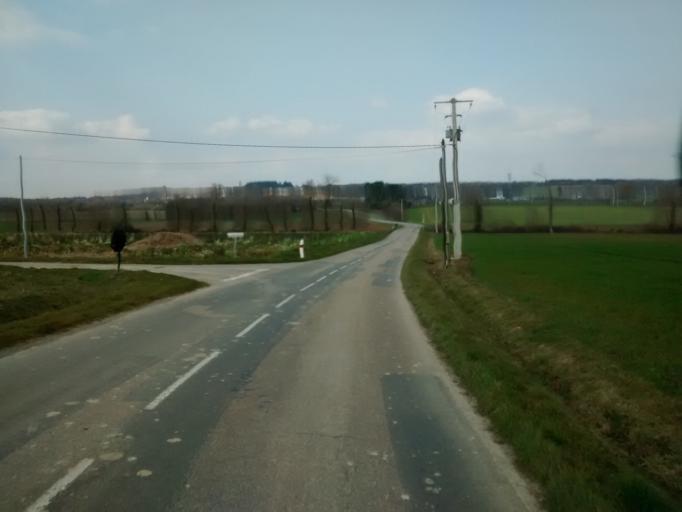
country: FR
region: Brittany
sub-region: Departement d'Ille-et-Vilaine
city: Maure-de-Bretagne
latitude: 47.9251
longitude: -1.9984
